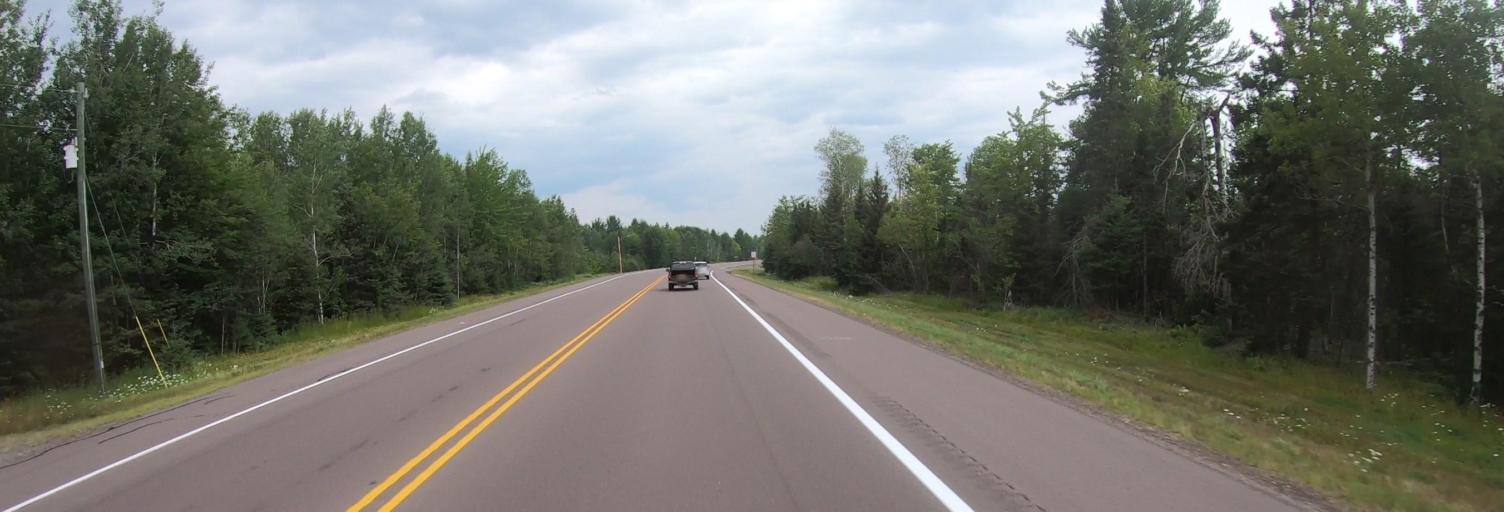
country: US
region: Michigan
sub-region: Baraga County
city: Baraga
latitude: 46.8793
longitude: -88.4788
